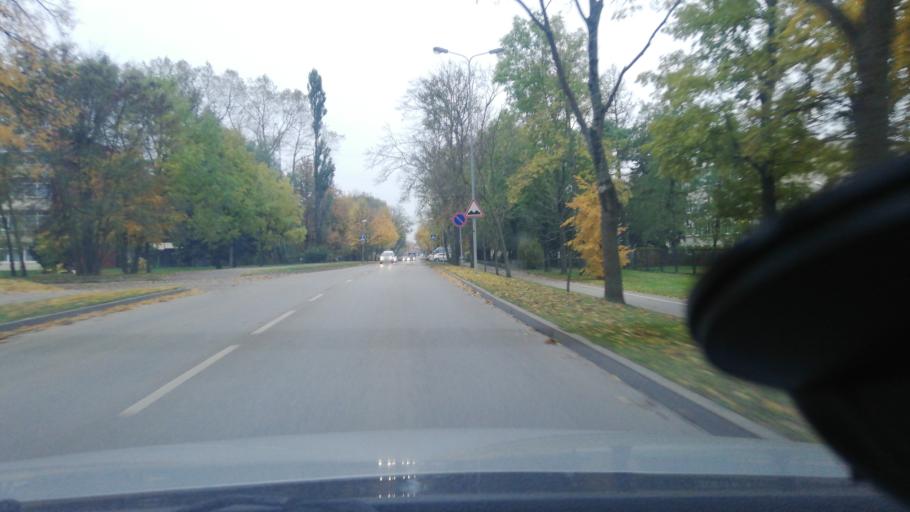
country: LT
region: Klaipedos apskritis
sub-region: Klaipeda
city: Klaipeda
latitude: 55.7279
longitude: 21.1318
